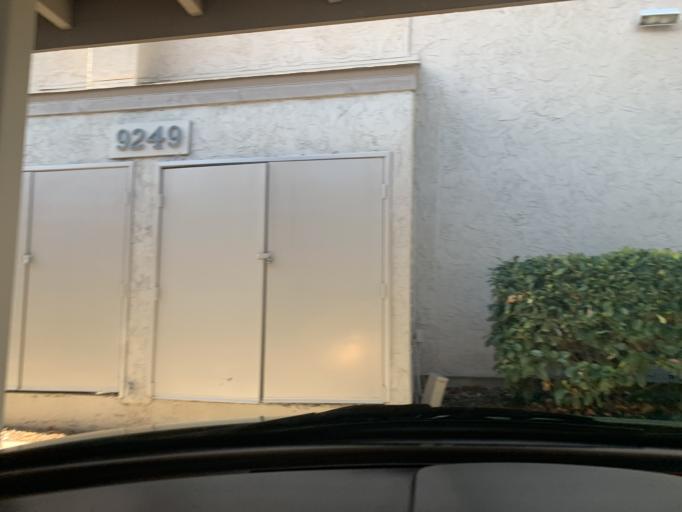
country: US
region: California
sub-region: San Diego County
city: San Diego
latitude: 32.8047
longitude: -117.1292
